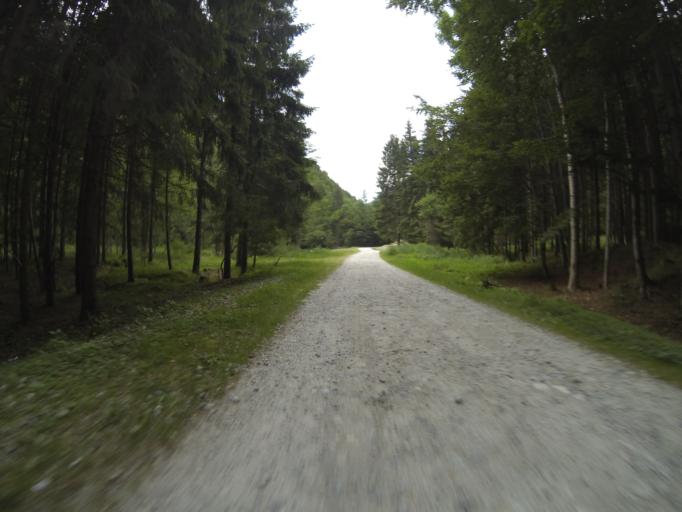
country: RO
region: Gorj
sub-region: Comuna Polovragi
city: Polovragi
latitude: 45.2477
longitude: 23.7660
